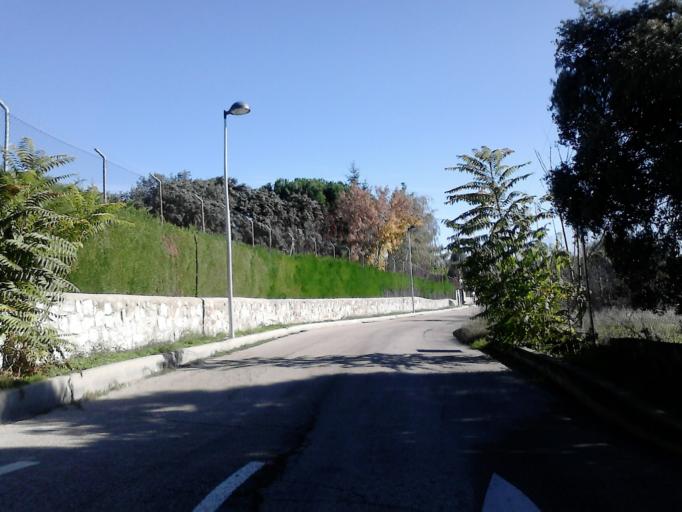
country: ES
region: Madrid
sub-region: Provincia de Madrid
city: Galapagar
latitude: 40.5701
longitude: -3.9979
